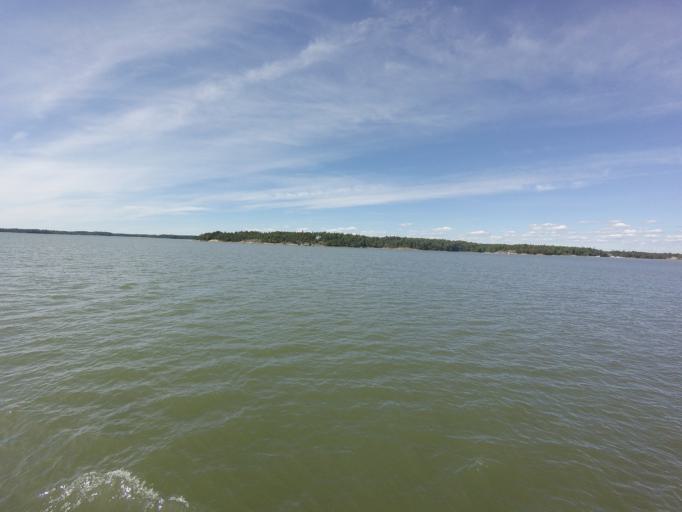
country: FI
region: Varsinais-Suomi
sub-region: Turku
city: Raisio
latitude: 60.4031
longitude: 22.1225
